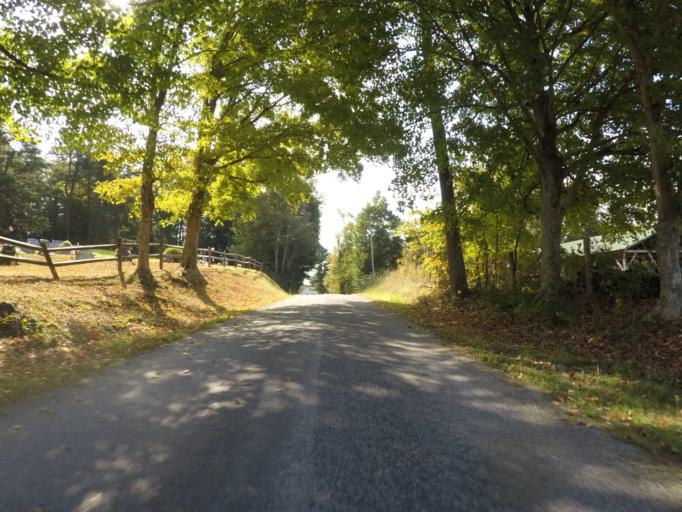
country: US
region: West Virginia
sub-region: Cabell County
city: Lesage
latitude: 38.6405
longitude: -82.4028
